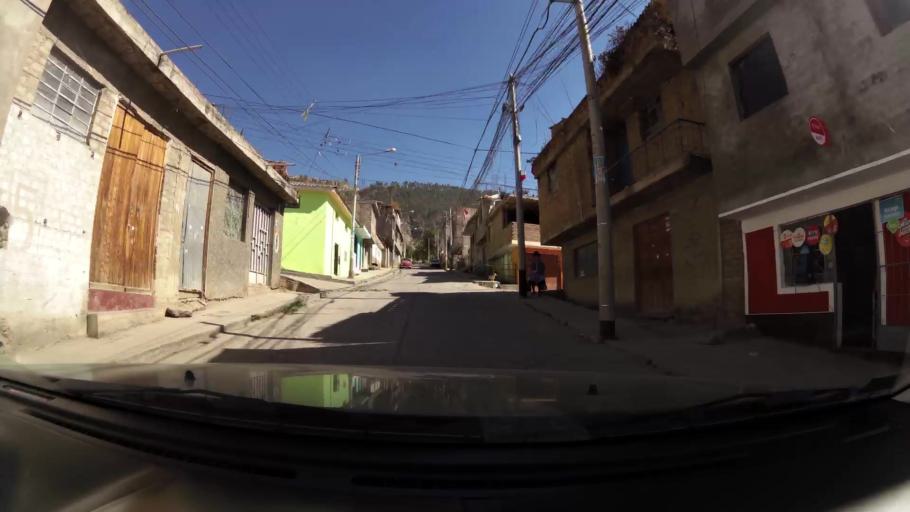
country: PE
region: Ayacucho
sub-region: Provincia de Huamanga
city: Ayacucho
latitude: -13.1579
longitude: -74.2316
